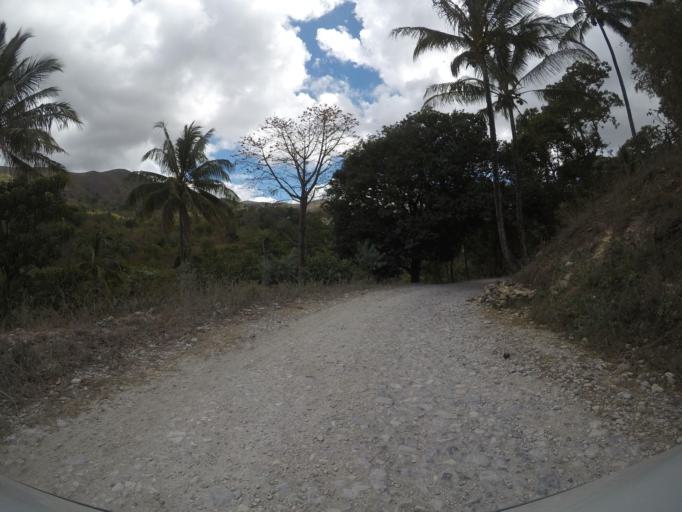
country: TL
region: Baucau
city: Baucau
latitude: -8.5258
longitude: 126.6928
